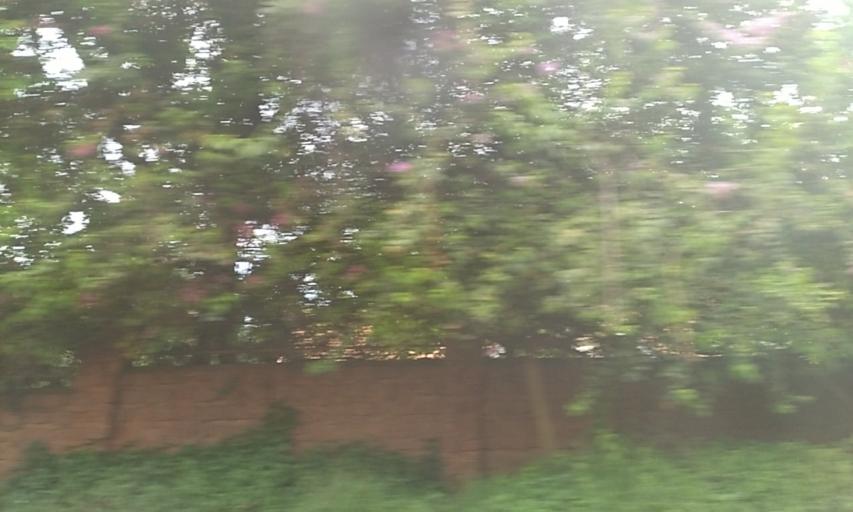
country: UG
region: Central Region
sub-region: Wakiso District
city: Bweyogerere
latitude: 0.3735
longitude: 32.6495
